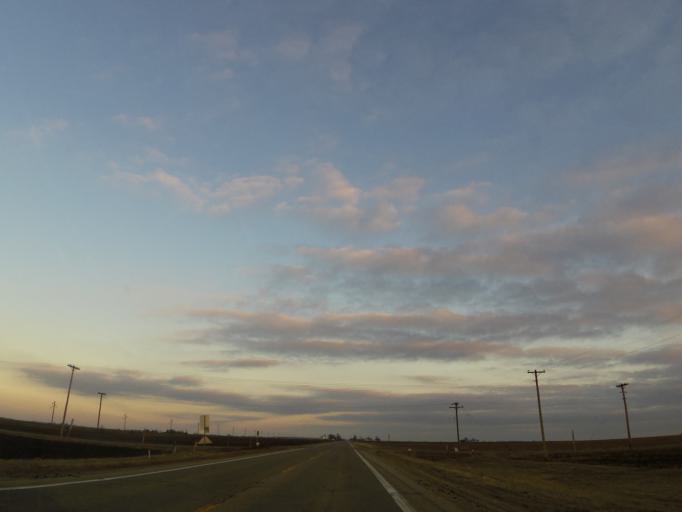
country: US
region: Illinois
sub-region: Woodford County
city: El Paso
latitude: 40.7382
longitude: -88.9685
